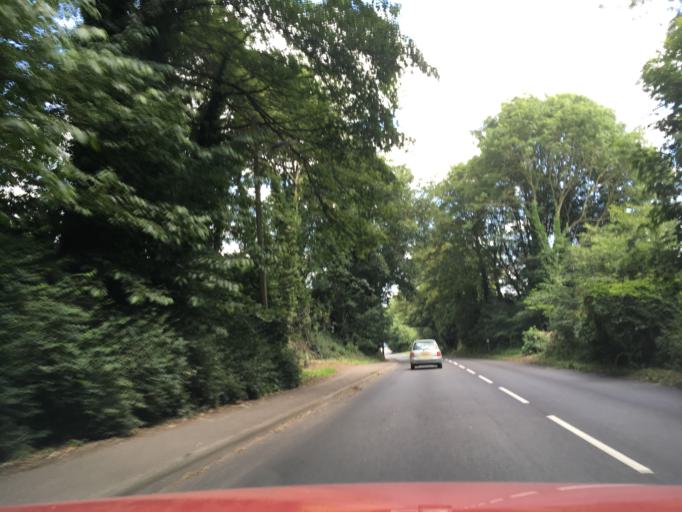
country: GB
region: England
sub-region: Gloucestershire
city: Dursley
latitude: 51.6993
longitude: -2.3670
